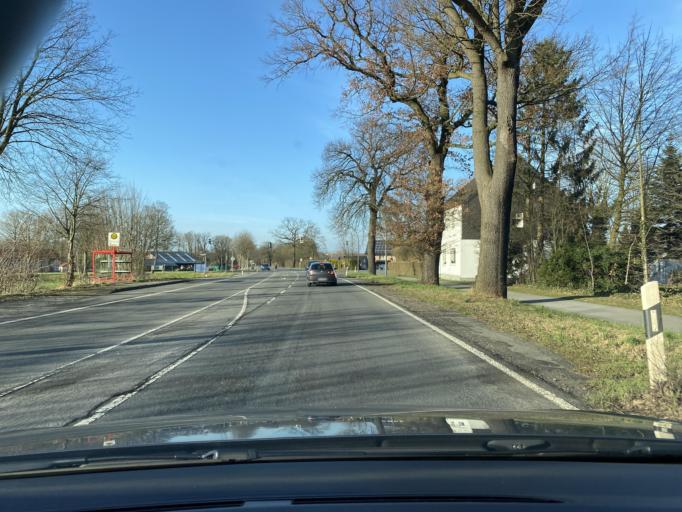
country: DE
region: North Rhine-Westphalia
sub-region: Regierungsbezirk Munster
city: Recklinghausen
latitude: 51.6440
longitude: 7.1884
